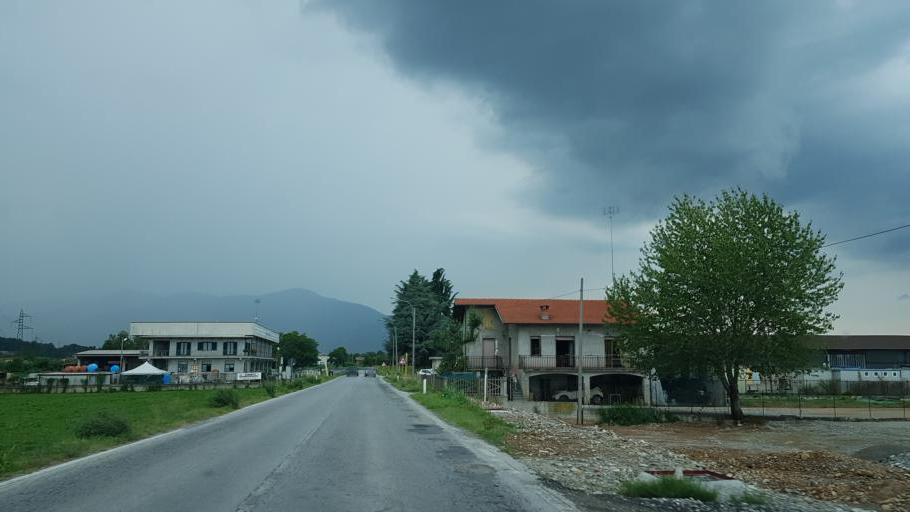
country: IT
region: Piedmont
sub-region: Provincia di Cuneo
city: Caraglio
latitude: 44.4309
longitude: 7.4238
